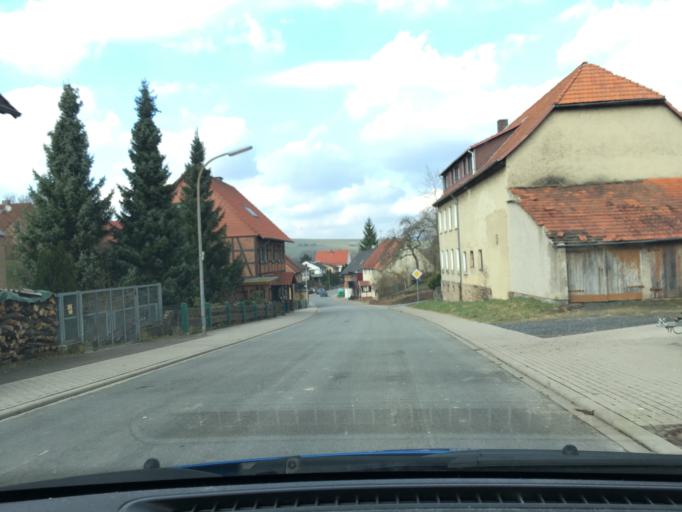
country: DE
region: Lower Saxony
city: Uslar
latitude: 51.6221
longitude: 9.6216
